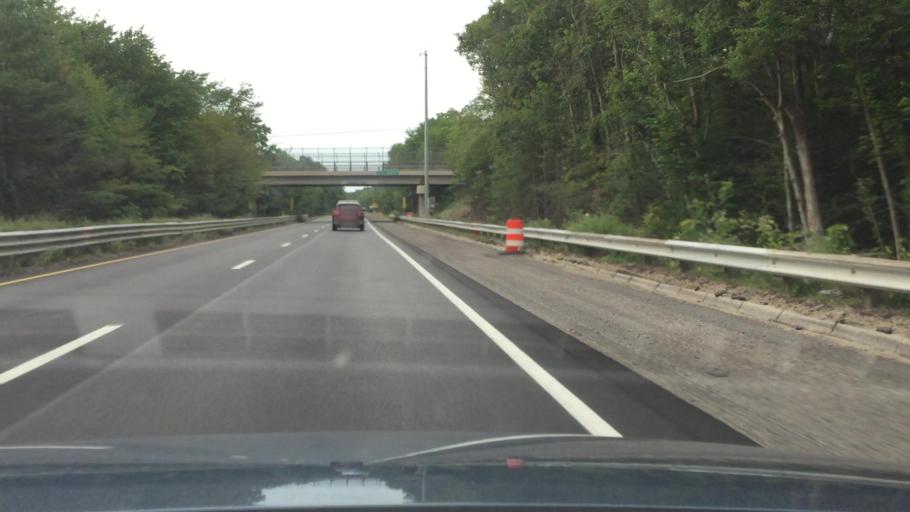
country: US
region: Massachusetts
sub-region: Plymouth County
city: Marshfield
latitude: 42.0545
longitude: -70.7247
